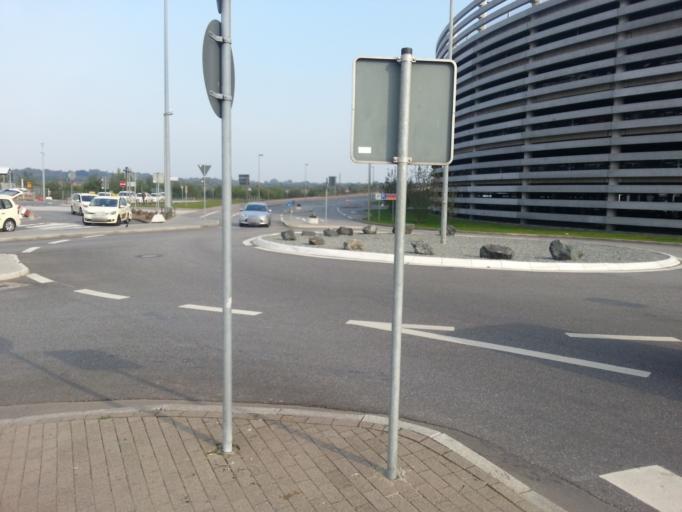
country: DE
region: Hamburg
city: Fuhlsbuettel
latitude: 53.6354
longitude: 10.0064
